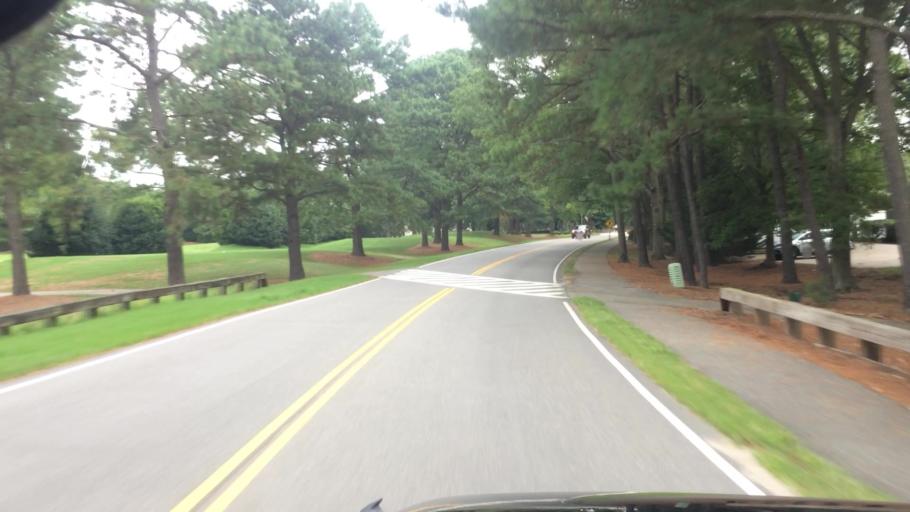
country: US
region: Virginia
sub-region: City of Williamsburg
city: Williamsburg
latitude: 37.2290
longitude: -76.6657
